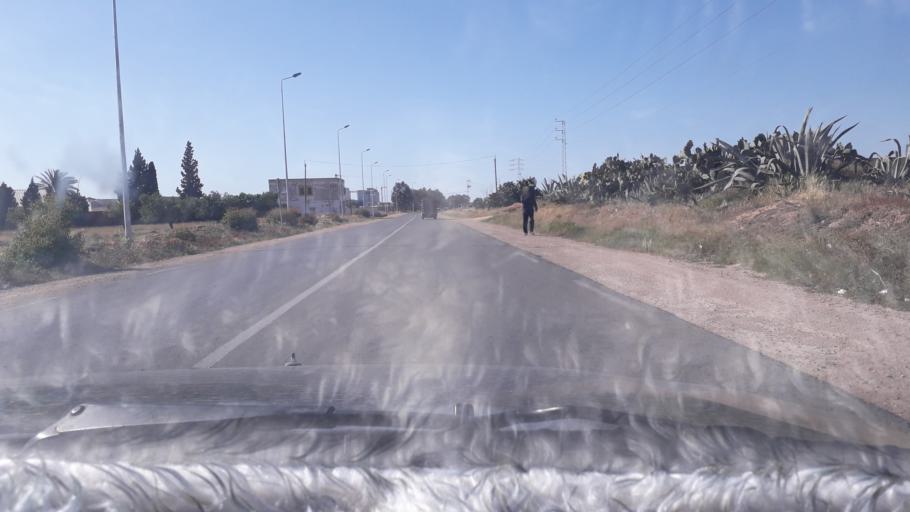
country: TN
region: Safaqis
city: Al Qarmadah
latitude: 34.8709
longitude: 10.7562
